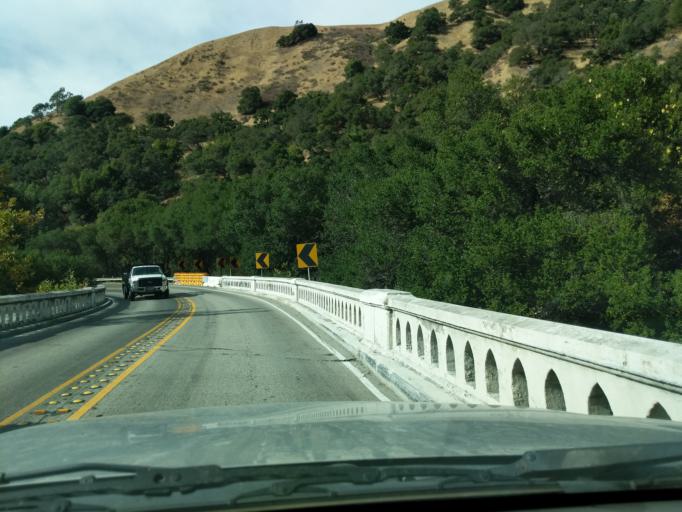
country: US
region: California
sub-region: Alameda County
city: Fremont
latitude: 37.5987
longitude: -121.9392
